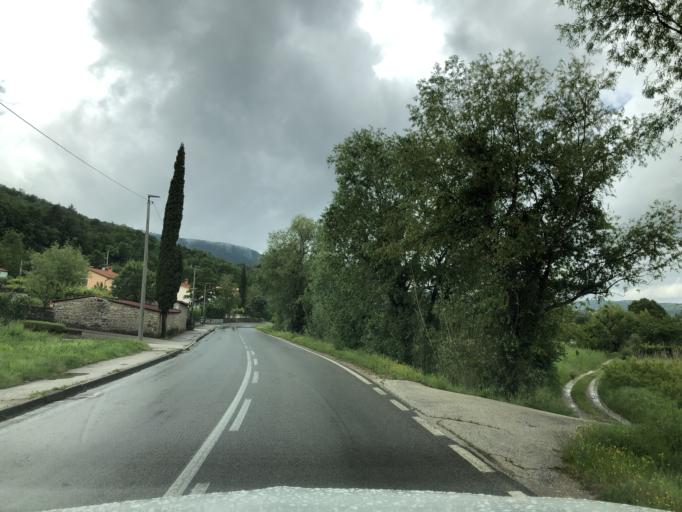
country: SI
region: Koper-Capodistria
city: Prade
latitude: 45.5177
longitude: 13.7746
